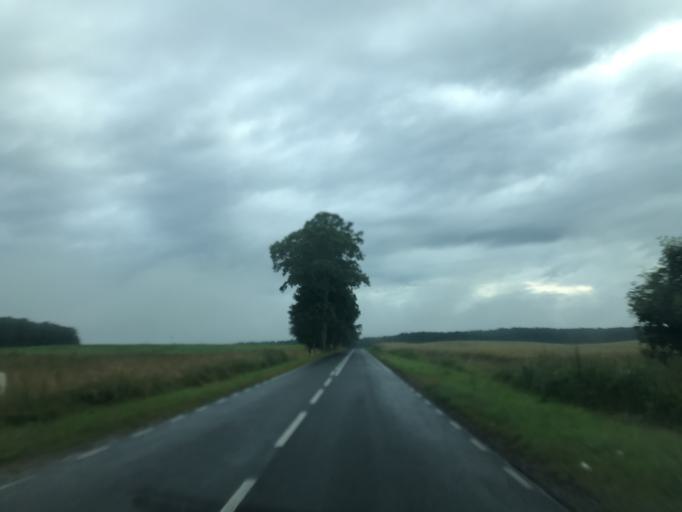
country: PL
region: West Pomeranian Voivodeship
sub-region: Powiat koszalinski
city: Bobolice
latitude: 53.9908
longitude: 16.4759
